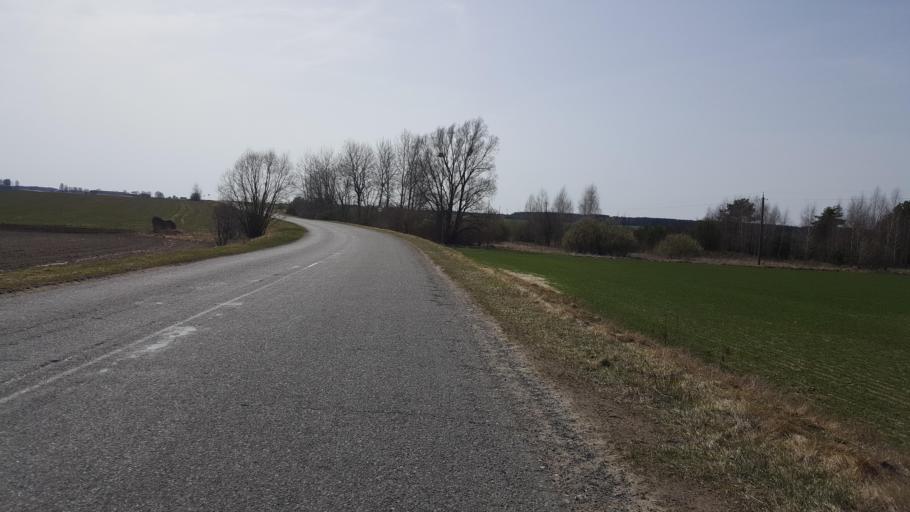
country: BY
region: Brest
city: Kamyanyets
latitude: 52.4703
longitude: 23.8574
